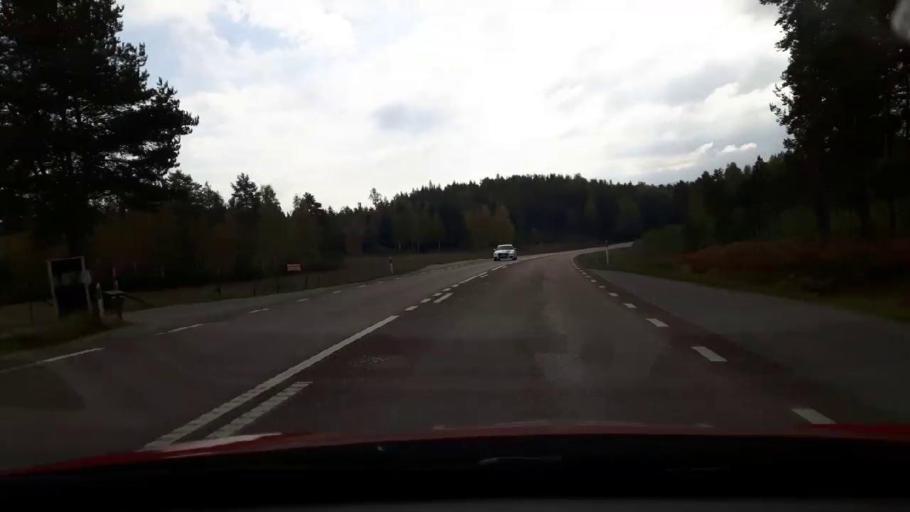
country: SE
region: Gaevleborg
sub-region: Bollnas Kommun
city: Kilafors
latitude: 61.2625
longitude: 16.5516
